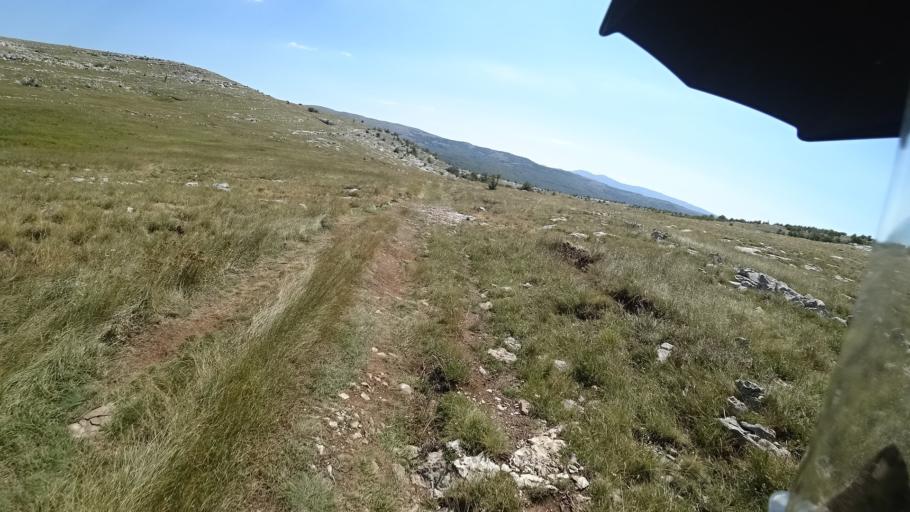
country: HR
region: Splitsko-Dalmatinska
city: Hrvace
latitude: 43.8977
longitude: 16.5895
